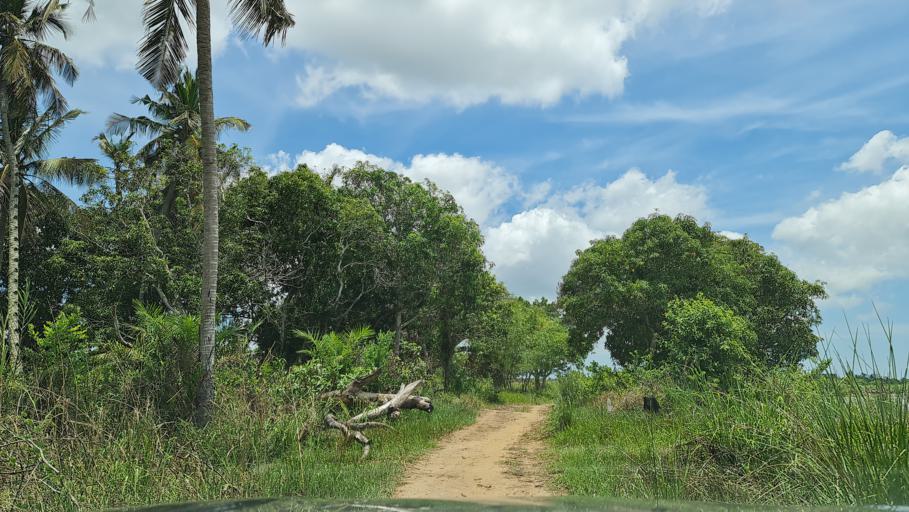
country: MZ
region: Zambezia
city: Quelimane
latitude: -17.5840
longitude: 37.3823
